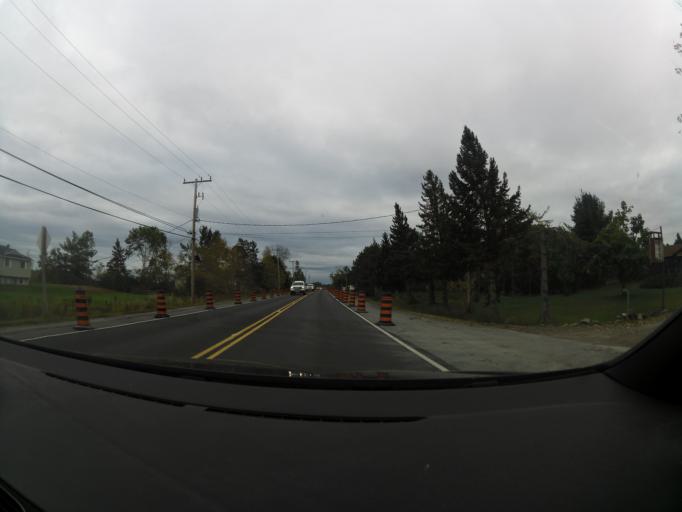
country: CA
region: Ontario
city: Bells Corners
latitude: 45.4210
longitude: -76.0187
